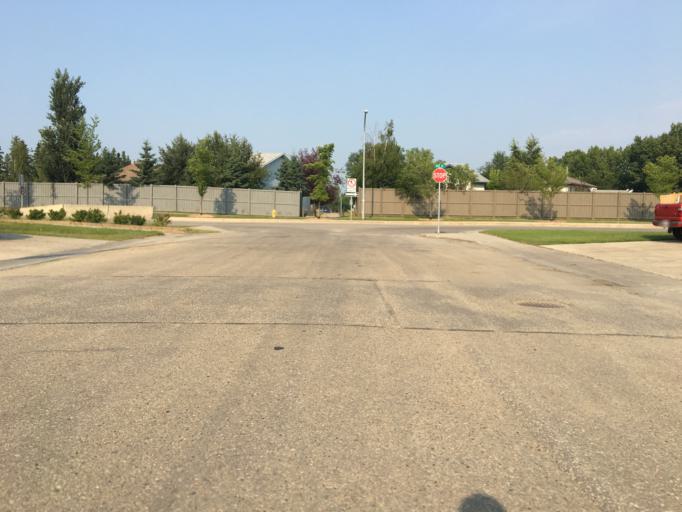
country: CA
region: Alberta
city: Grande Prairie
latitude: 55.1843
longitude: -118.8006
